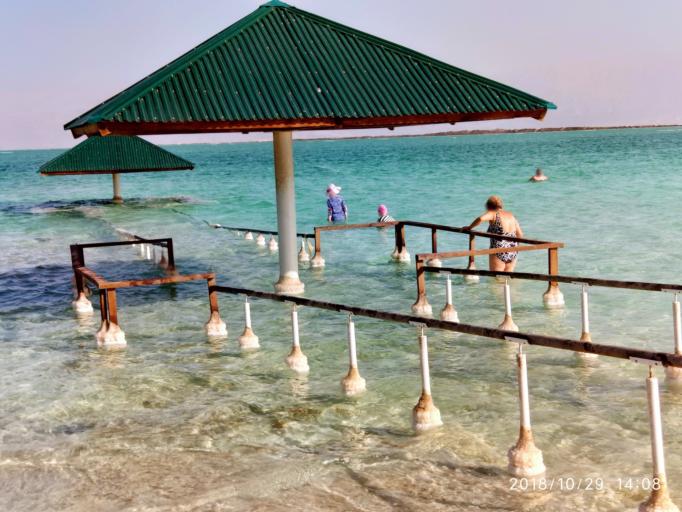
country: IL
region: Southern District
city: `En Boqeq
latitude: 31.1720
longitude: 35.3695
